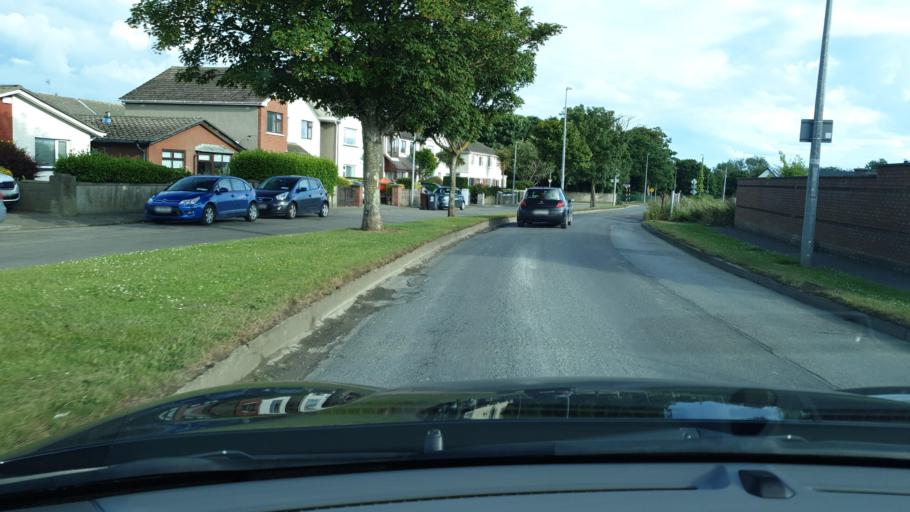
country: IE
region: Leinster
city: An Ros
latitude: 53.5276
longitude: -6.0981
